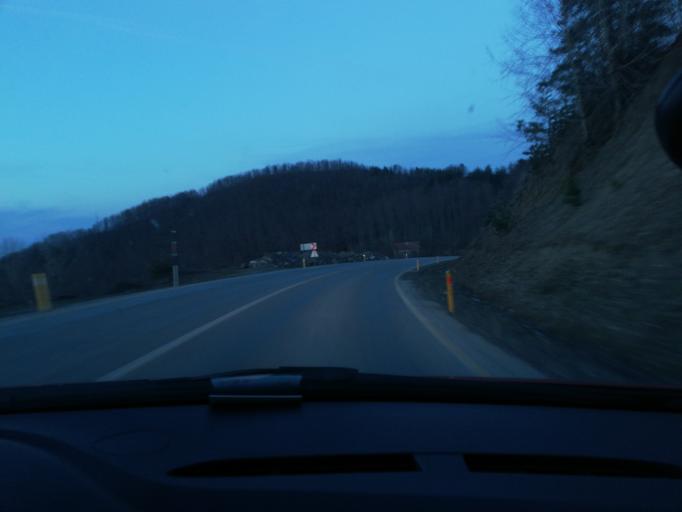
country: TR
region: Kastamonu
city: Inebolu
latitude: 41.9037
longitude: 33.7237
